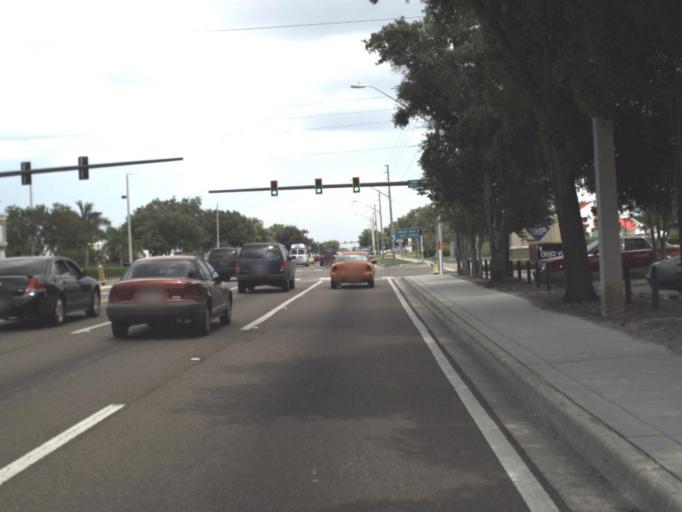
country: US
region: Florida
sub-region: Pinellas County
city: Saint Petersburg
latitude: 27.7876
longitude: -82.6794
